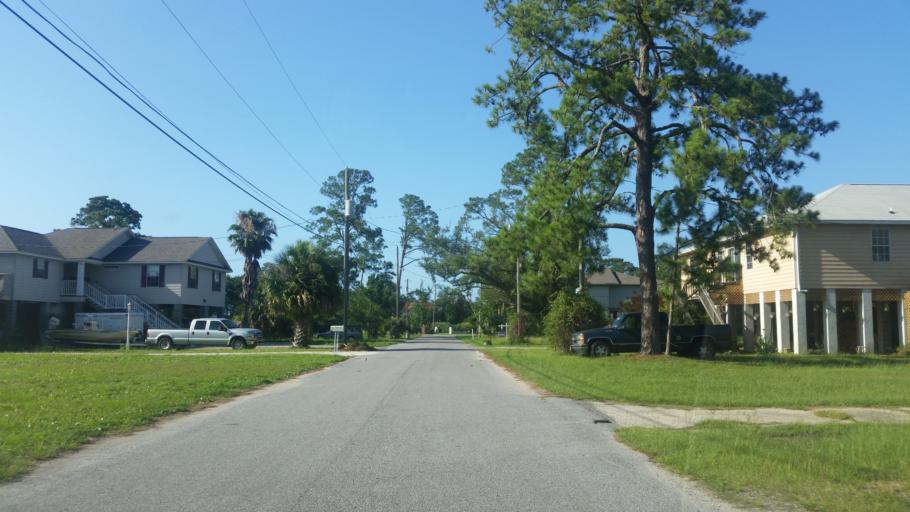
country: US
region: Florida
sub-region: Escambia County
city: Warrington
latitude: 30.3761
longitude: -87.2712
